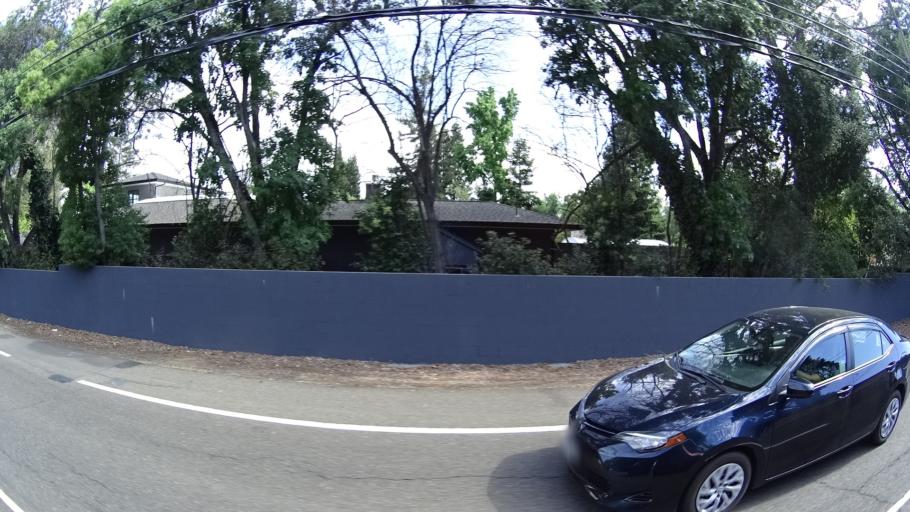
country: US
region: California
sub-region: Sacramento County
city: Arden-Arcade
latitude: 38.5741
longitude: -121.3896
